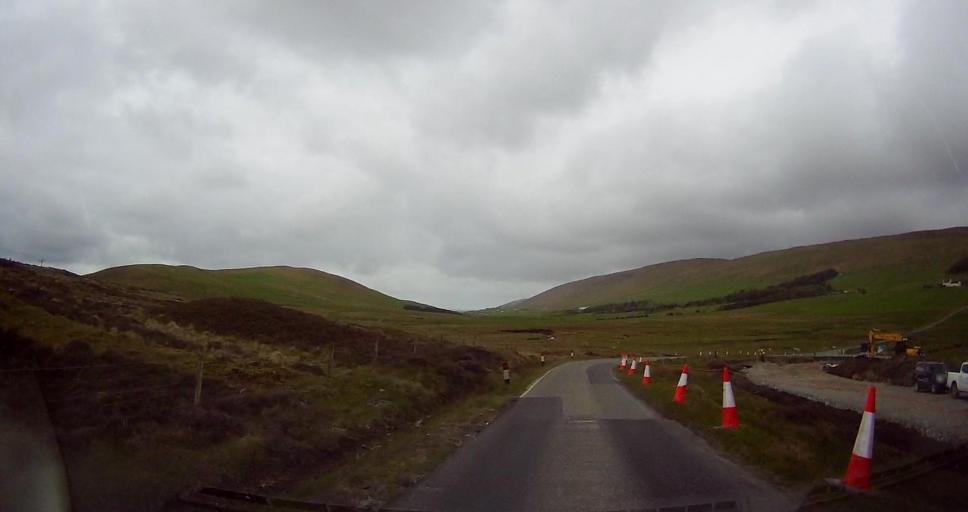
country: GB
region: Scotland
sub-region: Shetland Islands
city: Lerwick
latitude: 60.2768
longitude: -1.2729
